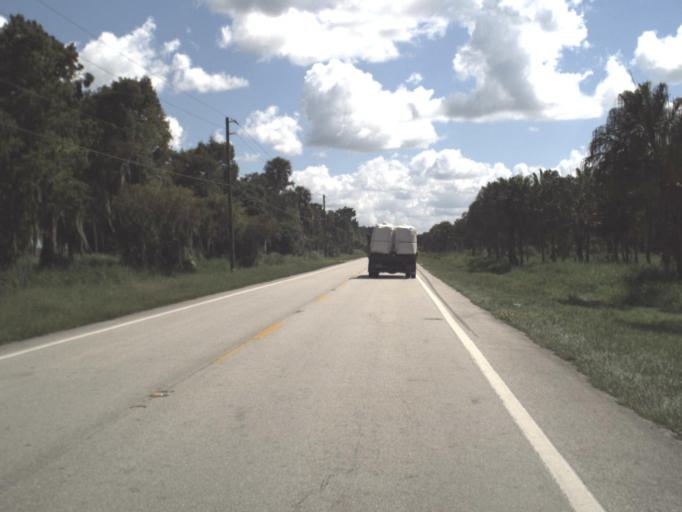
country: US
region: Florida
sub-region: Okeechobee County
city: Taylor Creek
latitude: 27.1619
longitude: -80.7127
